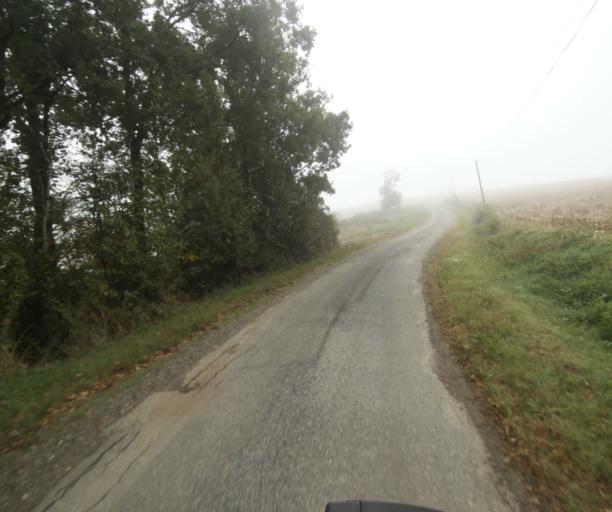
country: FR
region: Midi-Pyrenees
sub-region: Departement du Tarn-et-Garonne
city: Nohic
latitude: 43.9070
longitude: 1.4753
